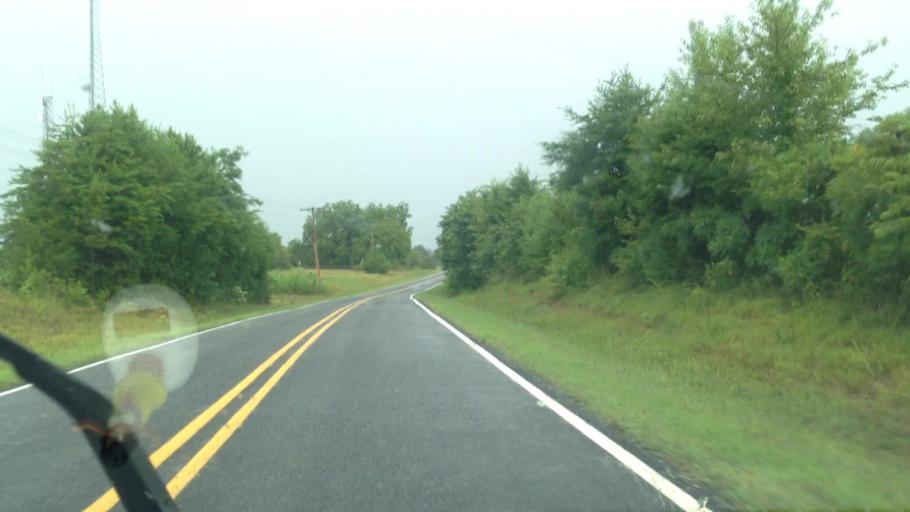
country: US
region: North Carolina
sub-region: Stokes County
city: Danbury
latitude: 36.4434
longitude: -80.0913
